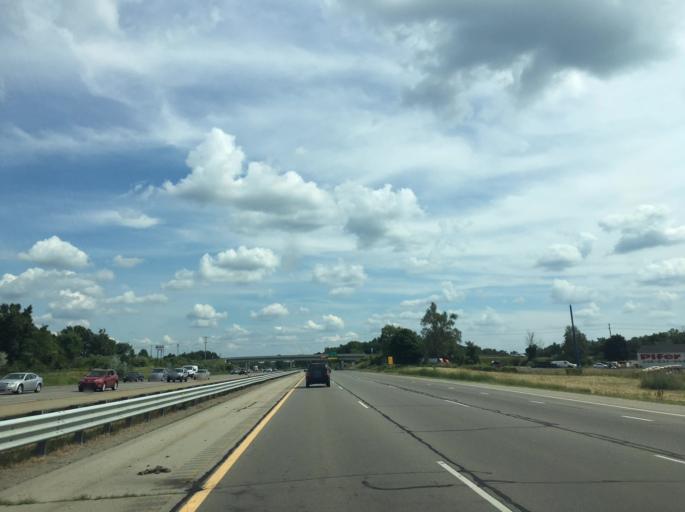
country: US
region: Michigan
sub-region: Oakland County
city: Holly
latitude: 42.7849
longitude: -83.5365
